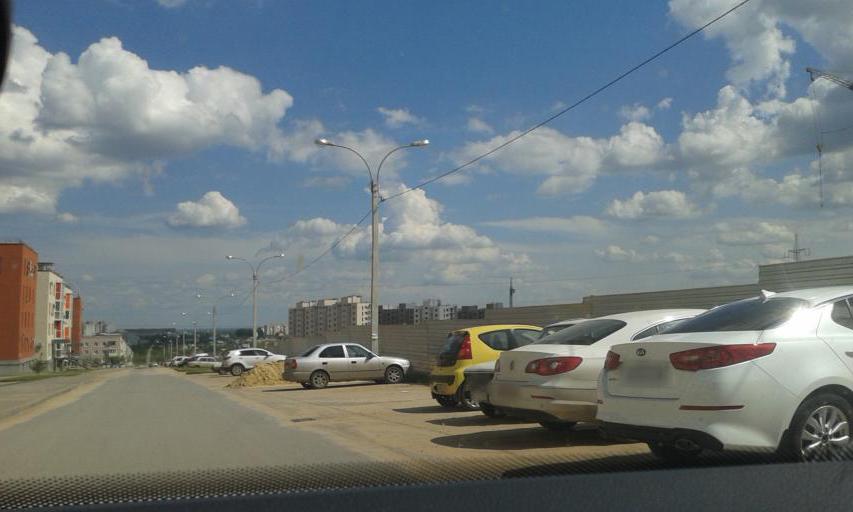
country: RU
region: Volgograd
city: Volgograd
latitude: 48.6634
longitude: 44.4122
